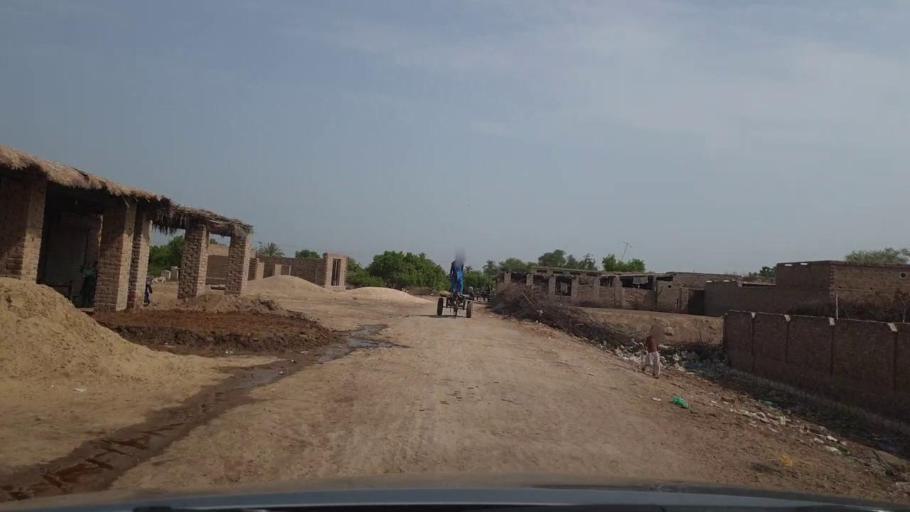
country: PK
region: Sindh
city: Rohri
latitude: 27.6456
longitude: 69.0236
